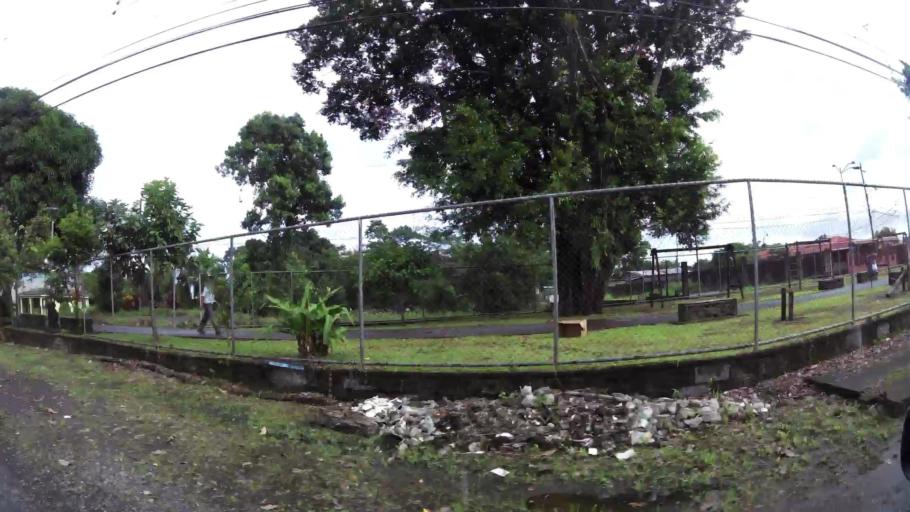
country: CR
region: Limon
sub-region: Canton de Pococi
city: Guapiles
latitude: 10.2122
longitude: -83.7822
